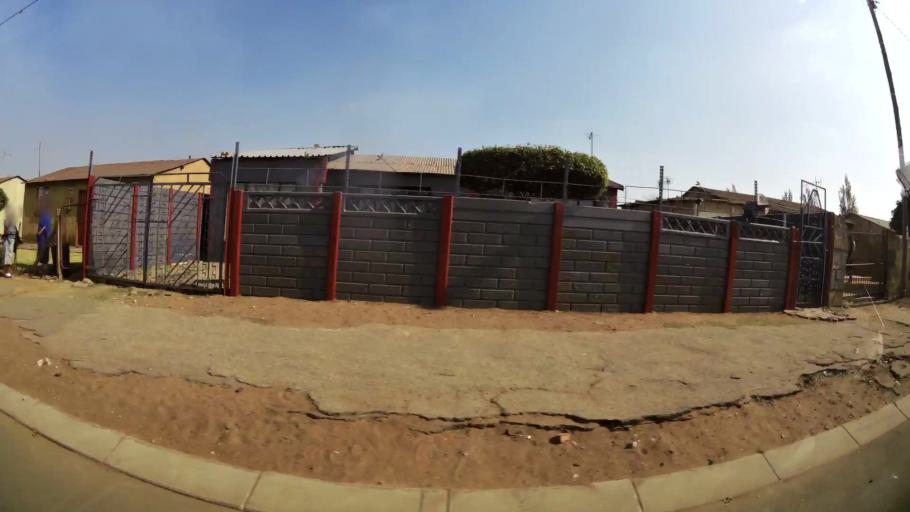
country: ZA
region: Gauteng
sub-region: Ekurhuleni Metropolitan Municipality
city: Brakpan
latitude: -26.1348
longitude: 28.4283
